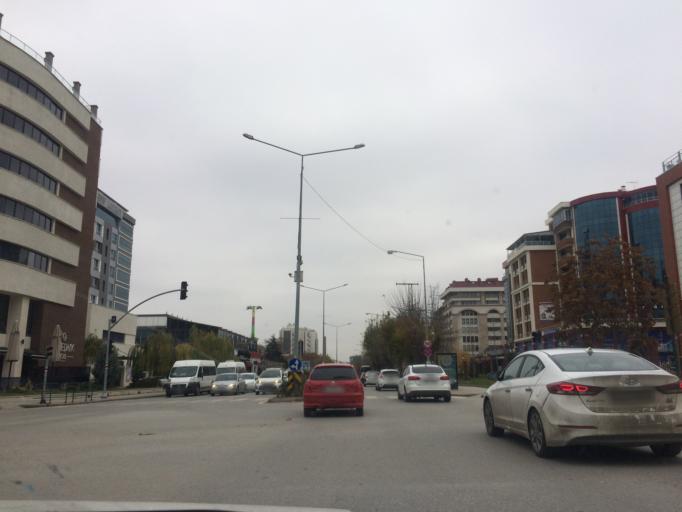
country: TR
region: Eskisehir
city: Eskisehir
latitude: 39.7850
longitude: 30.5016
